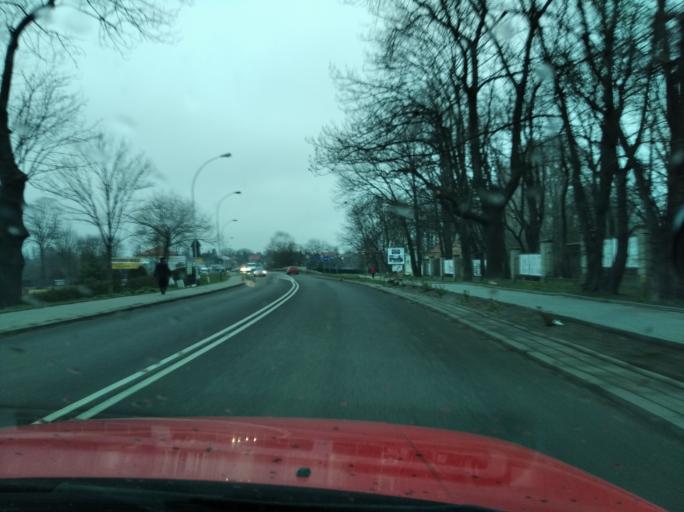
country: PL
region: Subcarpathian Voivodeship
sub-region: Powiat przeworski
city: Przeworsk
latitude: 50.0598
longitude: 22.4861
